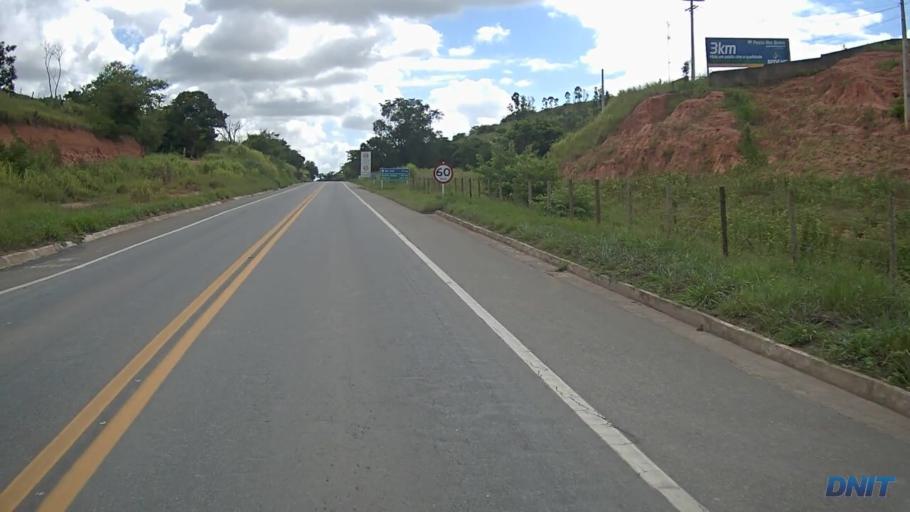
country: BR
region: Minas Gerais
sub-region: Governador Valadares
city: Governador Valadares
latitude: -18.9547
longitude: -42.0745
